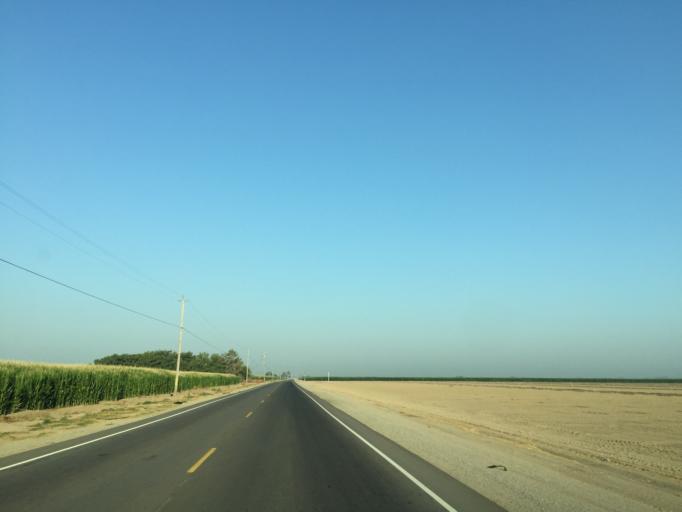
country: US
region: California
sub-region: Tulare County
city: Cutler
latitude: 36.4581
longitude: -119.3508
